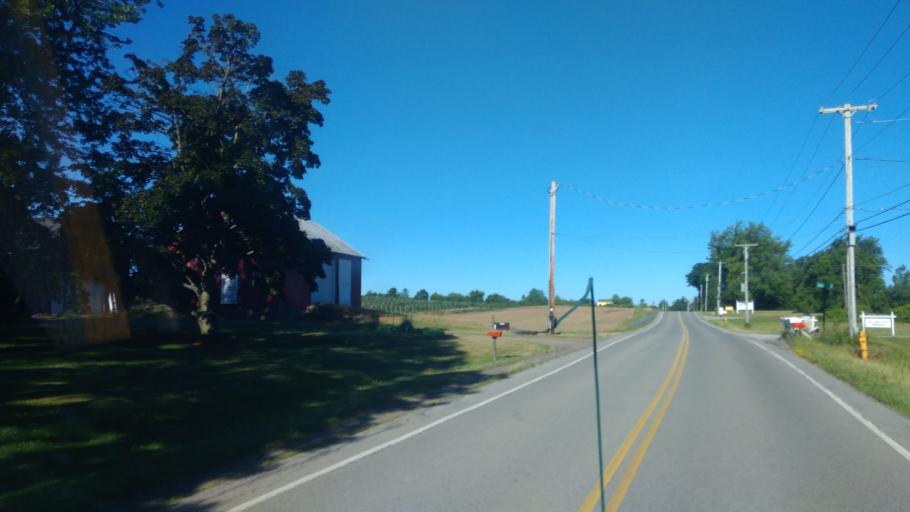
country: US
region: New York
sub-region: Wayne County
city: Williamson
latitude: 43.2838
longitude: -77.1427
